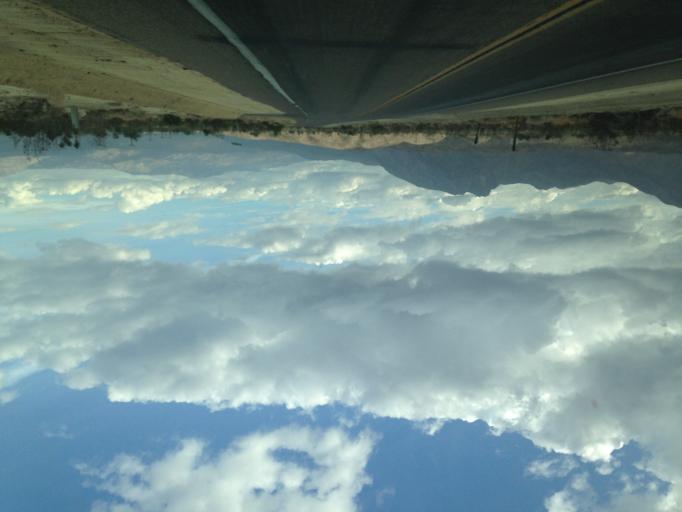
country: US
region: California
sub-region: San Diego County
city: Borrego Springs
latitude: 33.2212
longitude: -116.3739
